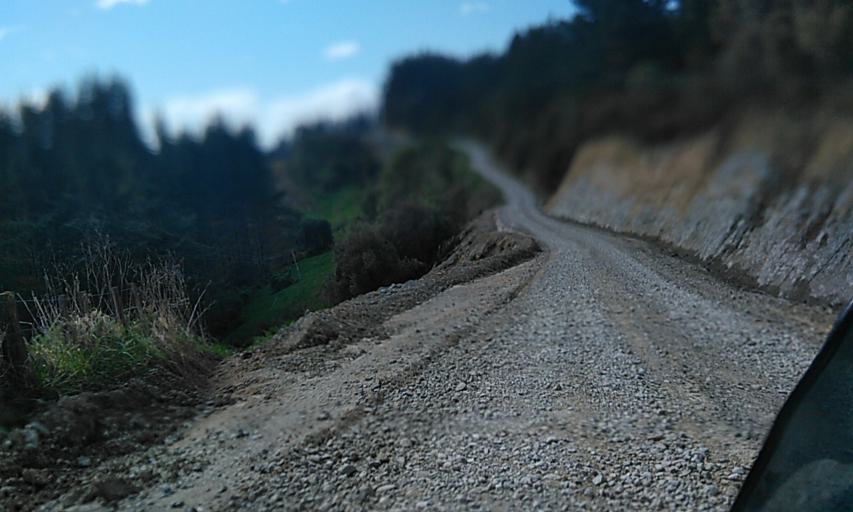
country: NZ
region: Gisborne
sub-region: Gisborne District
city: Gisborne
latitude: -38.3226
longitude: 178.0765
